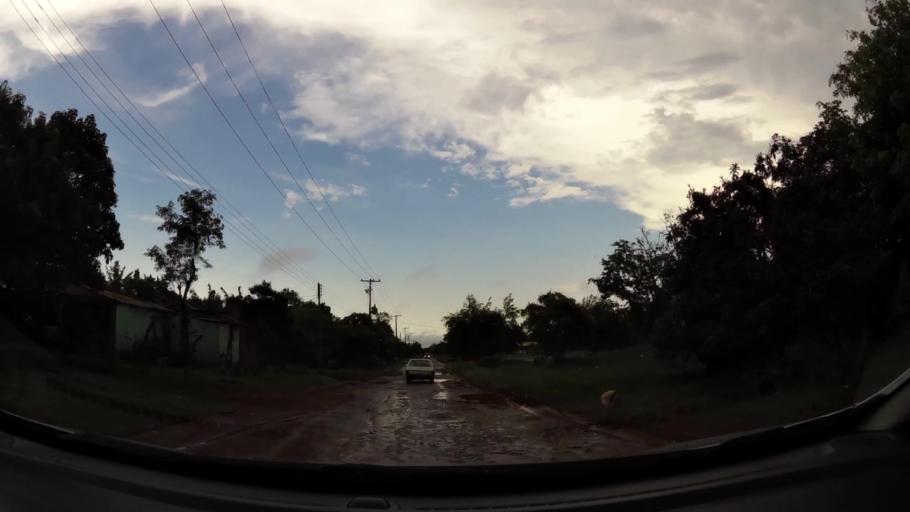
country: PY
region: Alto Parana
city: Presidente Franco
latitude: -25.5358
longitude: -54.6580
